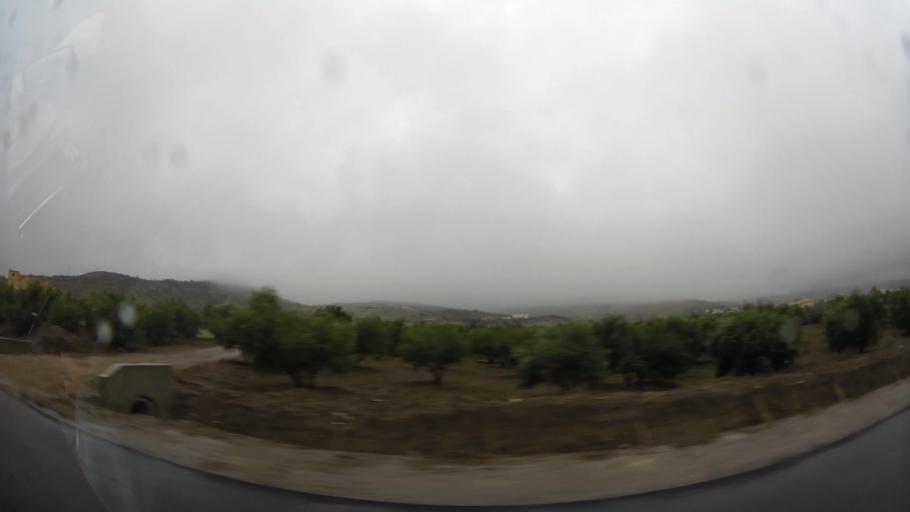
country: MA
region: Oriental
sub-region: Nador
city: Midar
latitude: 34.8355
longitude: -3.7202
